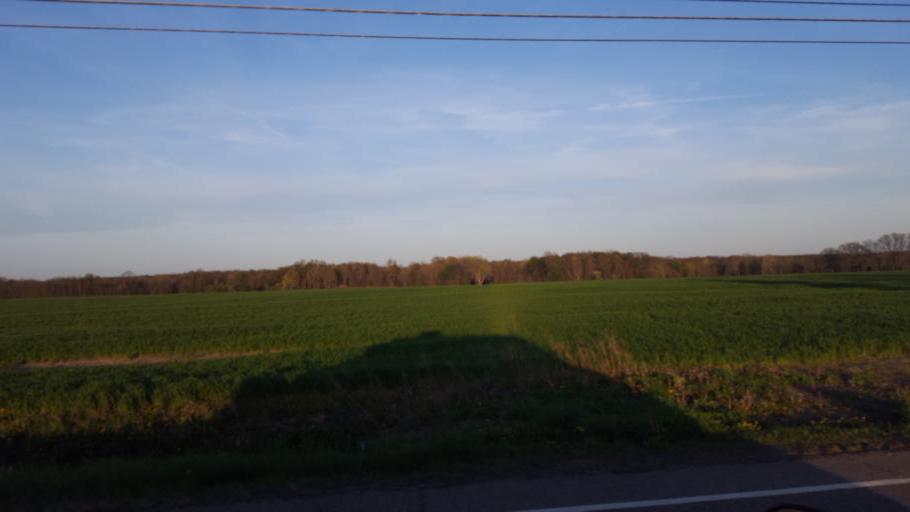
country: US
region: Ohio
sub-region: Ashtabula County
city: Andover
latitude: 41.4935
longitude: -80.5700
